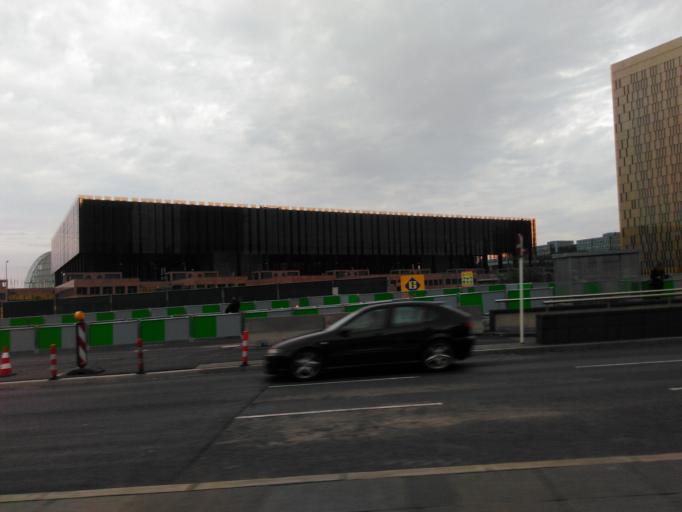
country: LU
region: Luxembourg
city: Kirchberg
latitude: 49.6193
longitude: 6.1421
